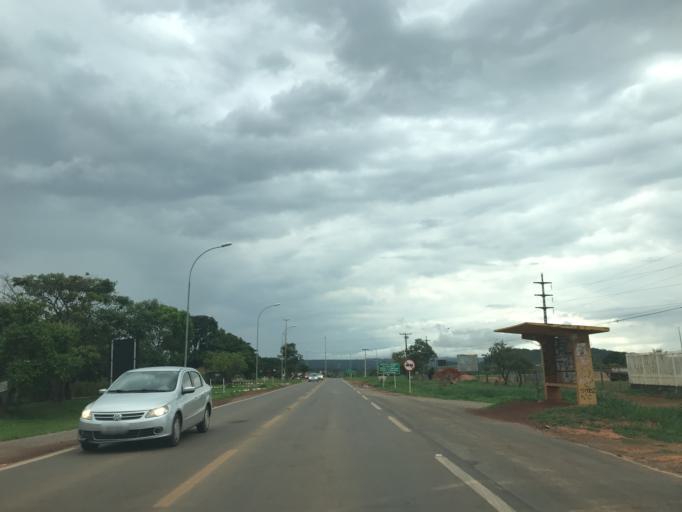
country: BR
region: Goias
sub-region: Planaltina
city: Planaltina
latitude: -15.6407
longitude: -47.6876
